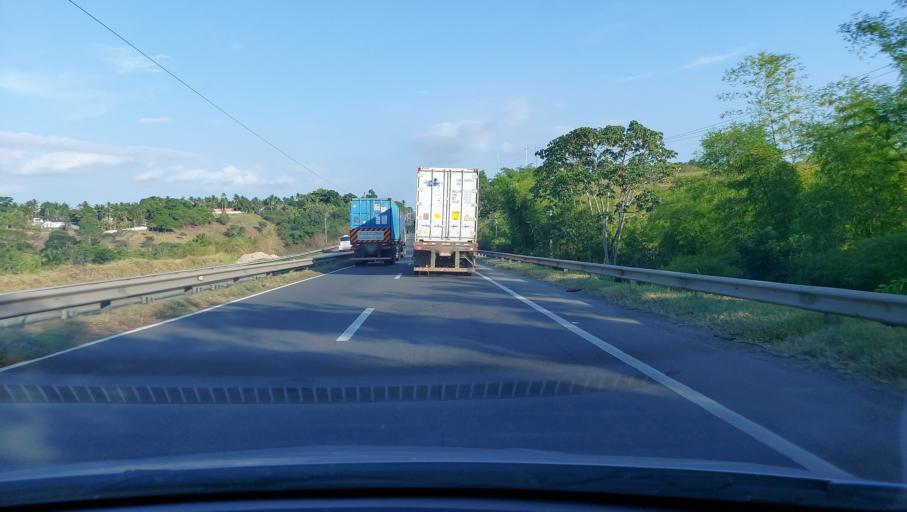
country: BR
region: Bahia
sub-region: Conceicao Do Jacuipe
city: Conceicao do Jacuipe
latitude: -12.3944
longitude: -38.7746
